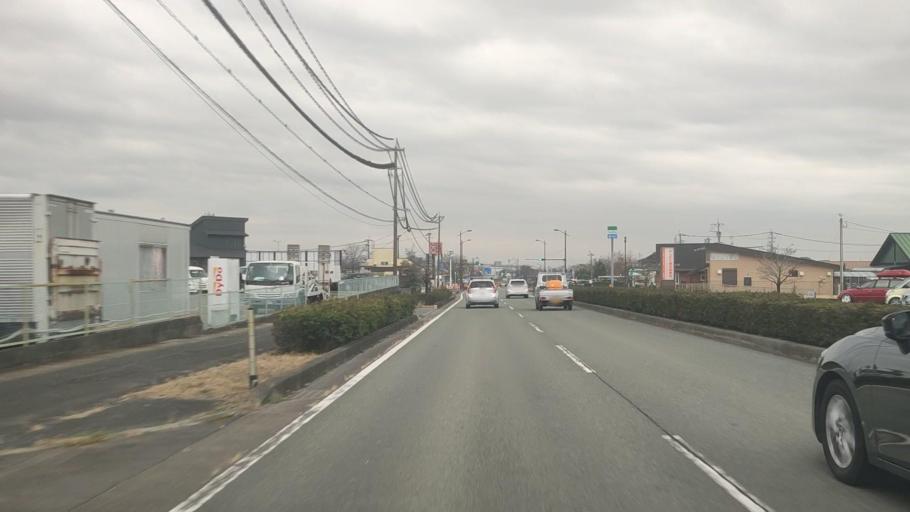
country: JP
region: Kumamoto
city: Ozu
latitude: 32.8320
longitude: 130.7992
